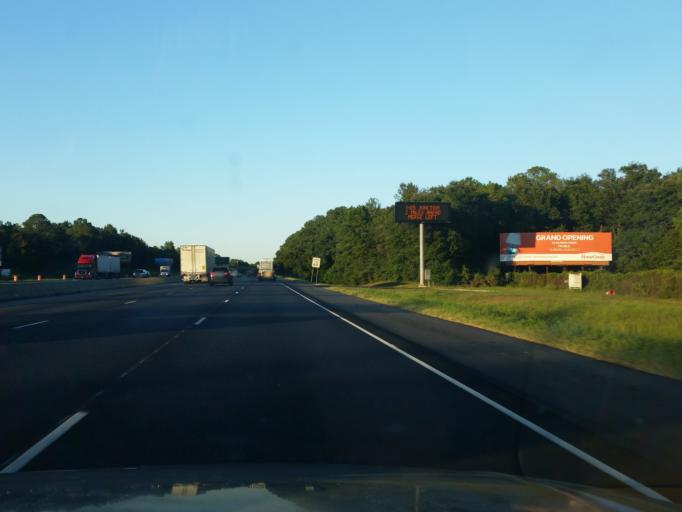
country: US
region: Alabama
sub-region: Mobile County
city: Tillmans Corner
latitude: 30.6123
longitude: -88.1416
